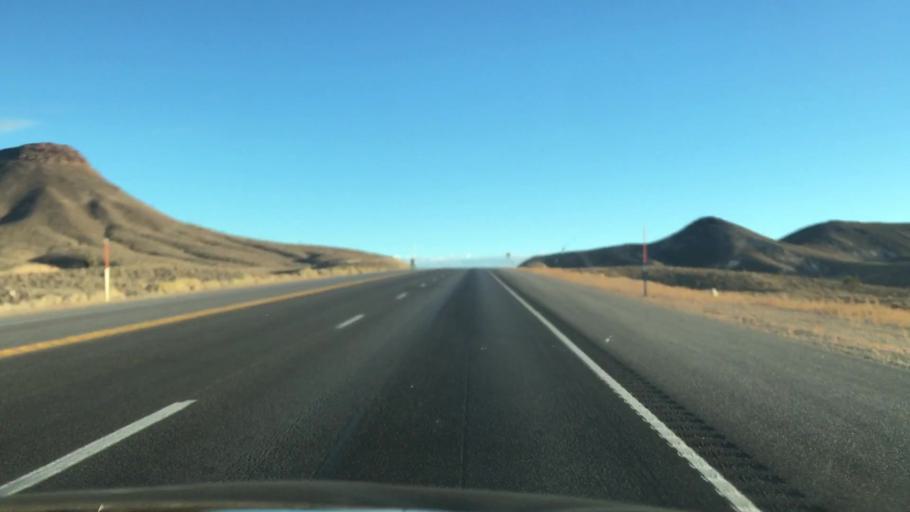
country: US
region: Nevada
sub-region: Esmeralda County
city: Goldfield
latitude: 37.6848
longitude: -117.2313
